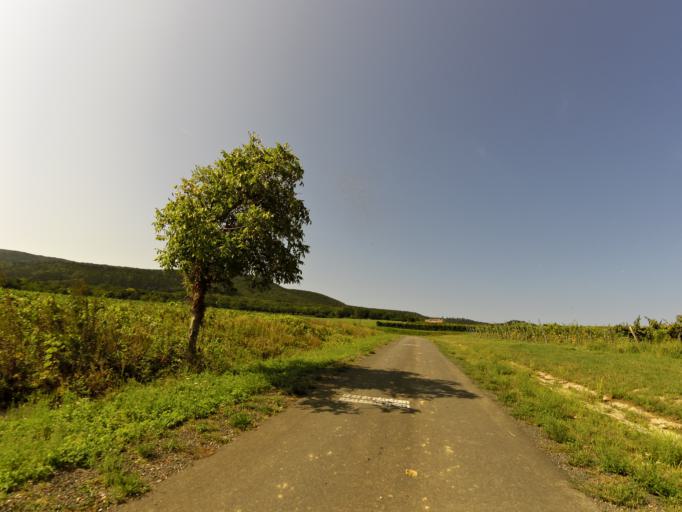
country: HU
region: Zala
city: Vonyarcvashegy
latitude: 46.8296
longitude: 17.3663
